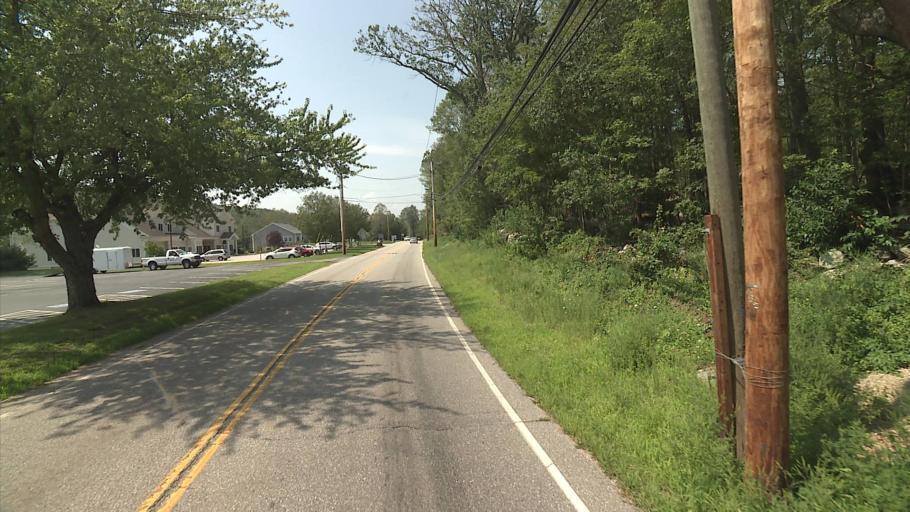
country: US
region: Connecticut
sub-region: New London County
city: Montville Center
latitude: 41.5061
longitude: -72.1423
